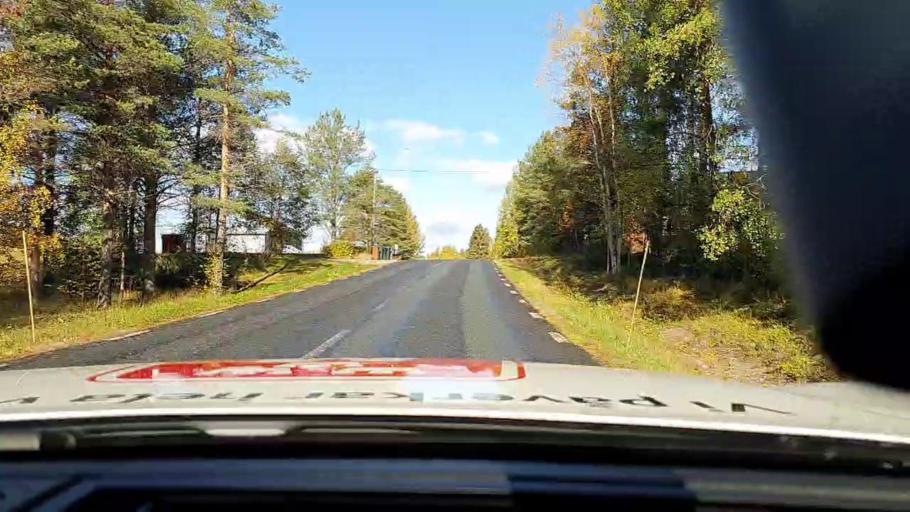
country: SE
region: Vaesterbotten
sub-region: Skelleftea Kommun
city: Langsele
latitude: 65.0034
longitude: 20.0909
